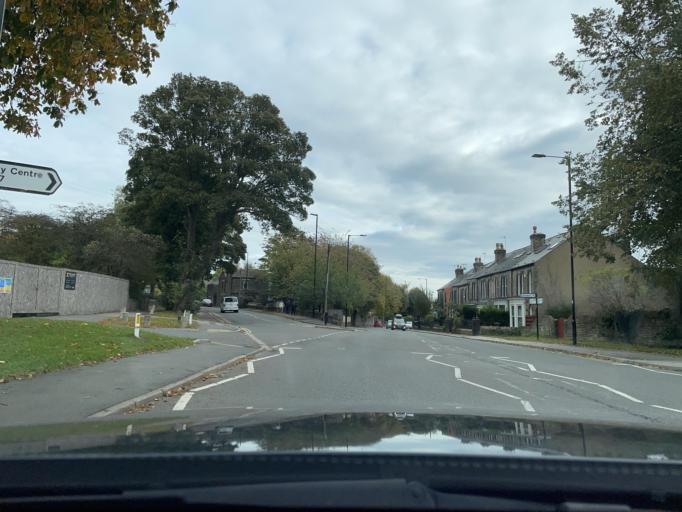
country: GB
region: England
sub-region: Sheffield
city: Sheffield
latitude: 53.3799
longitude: -1.5193
